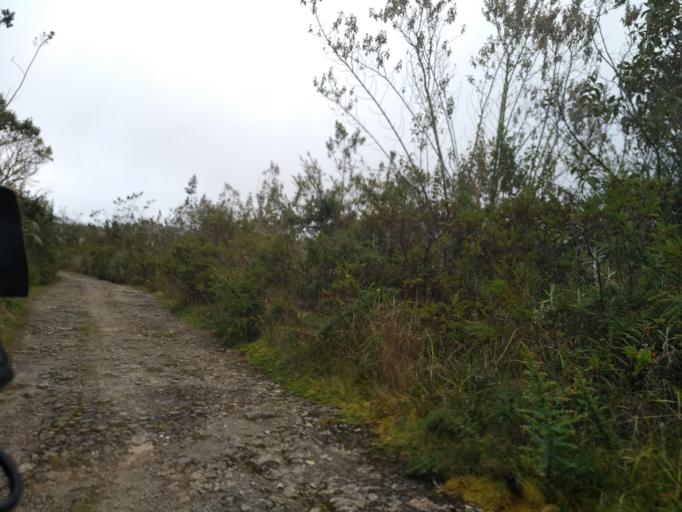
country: EC
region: Carchi
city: San Gabriel
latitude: 0.7010
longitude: -77.8430
